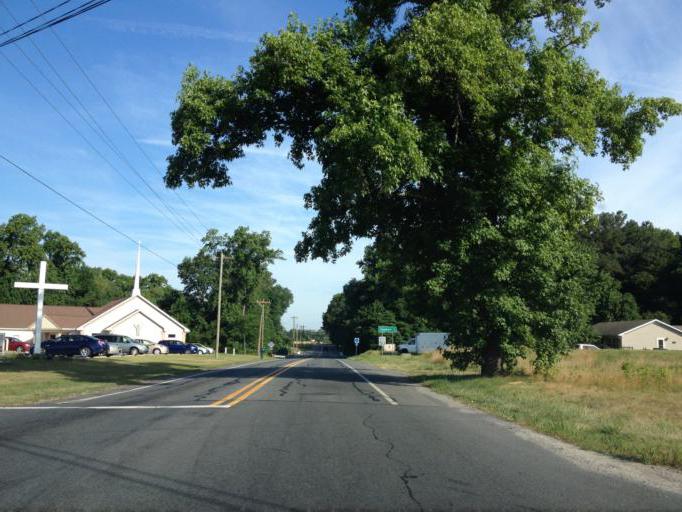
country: US
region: Delaware
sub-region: Sussex County
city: Selbyville
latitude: 38.5276
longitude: -75.2004
